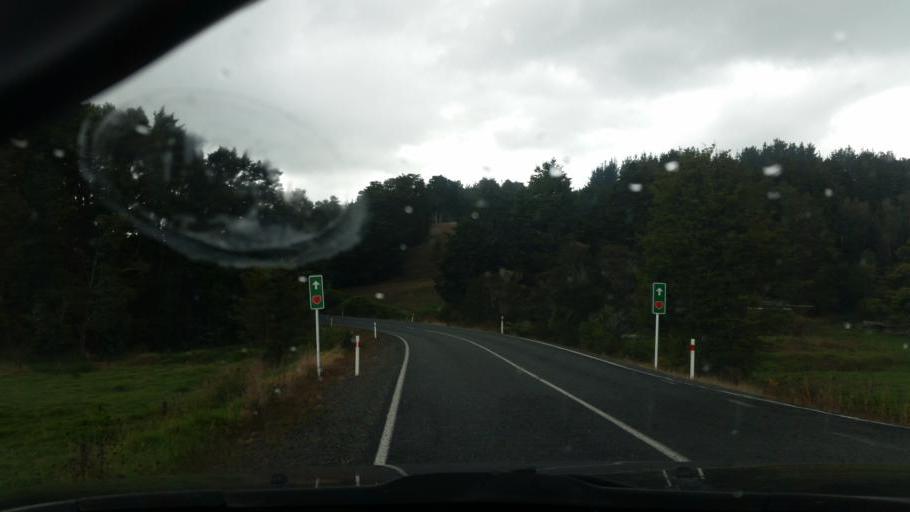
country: NZ
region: Northland
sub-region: Whangarei
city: Ruakaka
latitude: -35.9425
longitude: 174.2922
